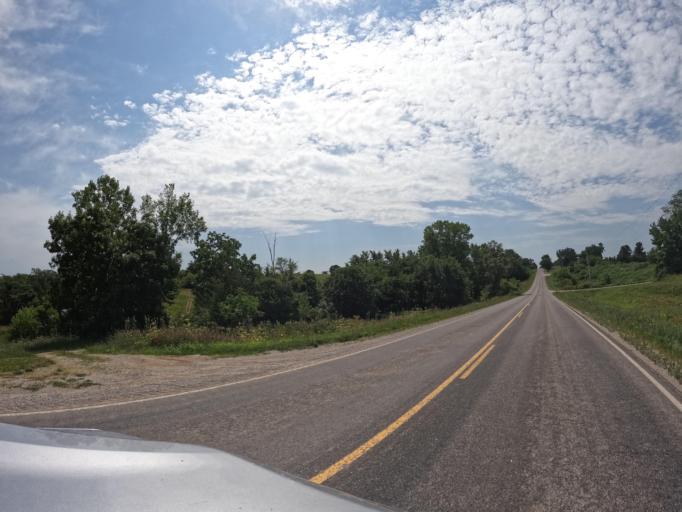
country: US
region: Iowa
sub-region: Appanoose County
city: Centerville
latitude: 40.7927
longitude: -92.9447
